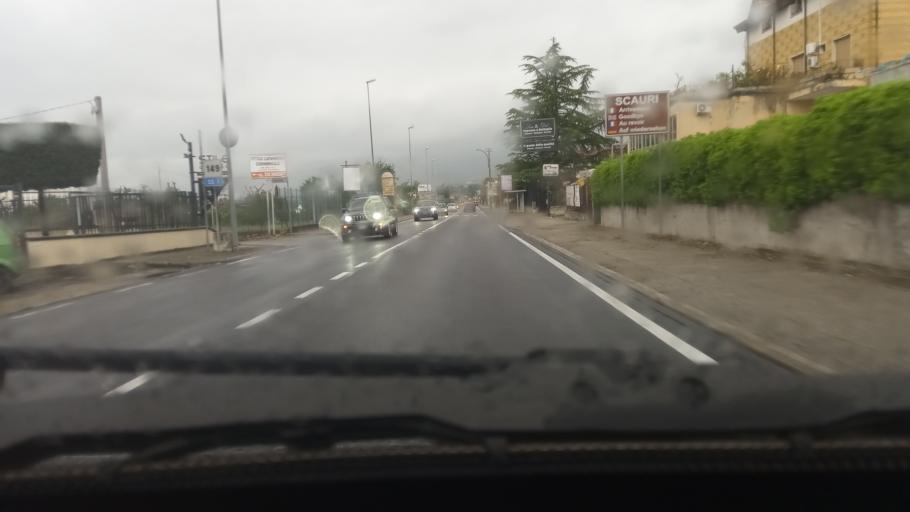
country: IT
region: Latium
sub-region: Provincia di Latina
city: Penitro
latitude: 41.2610
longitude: 13.6890
